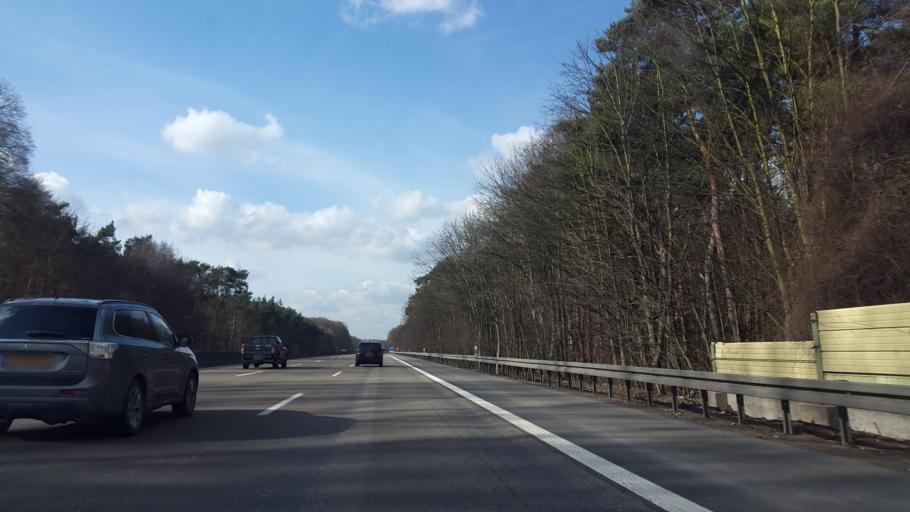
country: DE
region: Hesse
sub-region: Regierungsbezirk Darmstadt
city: Seligenstadt
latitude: 50.0112
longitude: 8.9735
